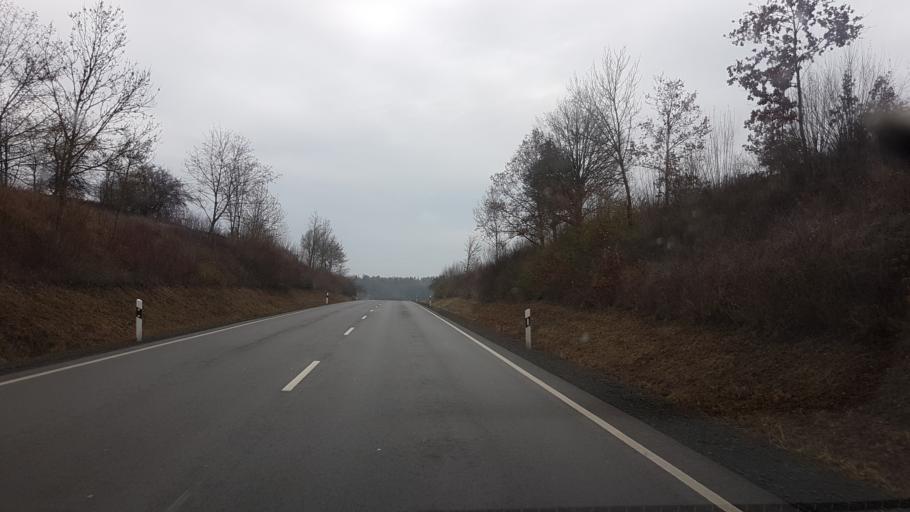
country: DE
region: Bavaria
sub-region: Regierungsbezirk Unterfranken
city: Bundorf
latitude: 50.2604
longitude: 10.5430
